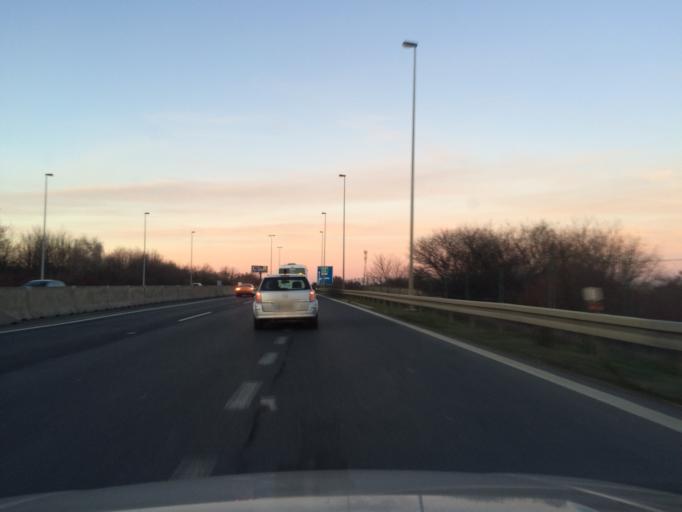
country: CZ
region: Central Bohemia
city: Hostivice
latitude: 50.0963
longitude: 14.2961
